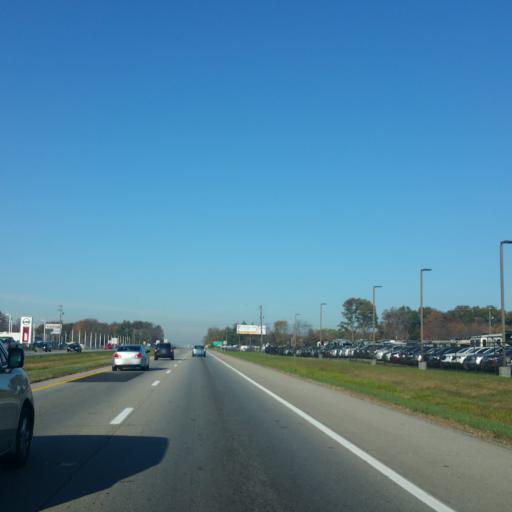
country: US
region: Ohio
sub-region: Clermont County
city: Summerside
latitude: 39.0915
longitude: -84.2502
